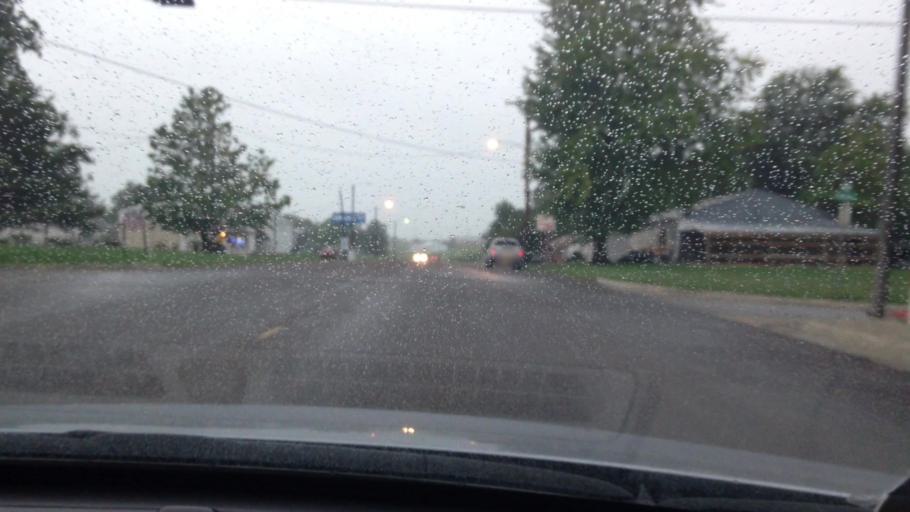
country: US
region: Kansas
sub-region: Brown County
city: Hiawatha
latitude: 39.8529
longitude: -95.5455
